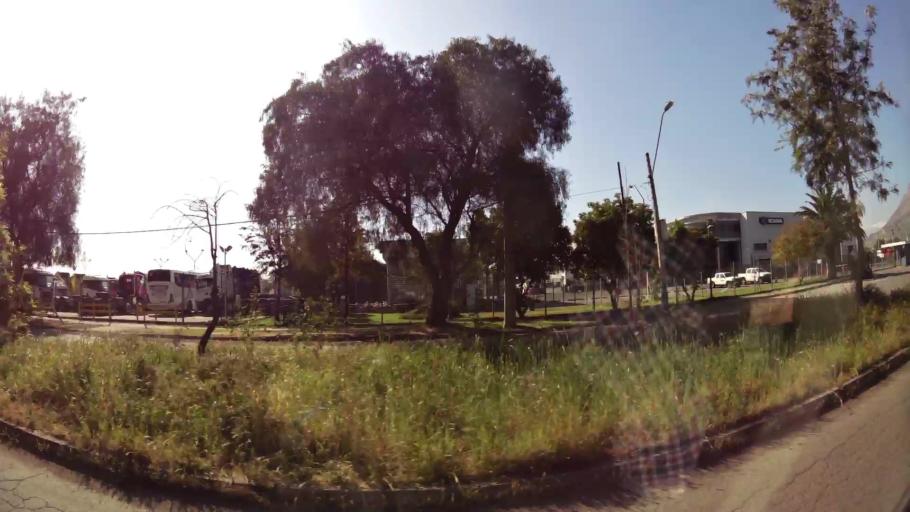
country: CL
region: Santiago Metropolitan
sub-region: Provincia de Chacabuco
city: Chicureo Abajo
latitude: -33.3310
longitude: -70.7182
